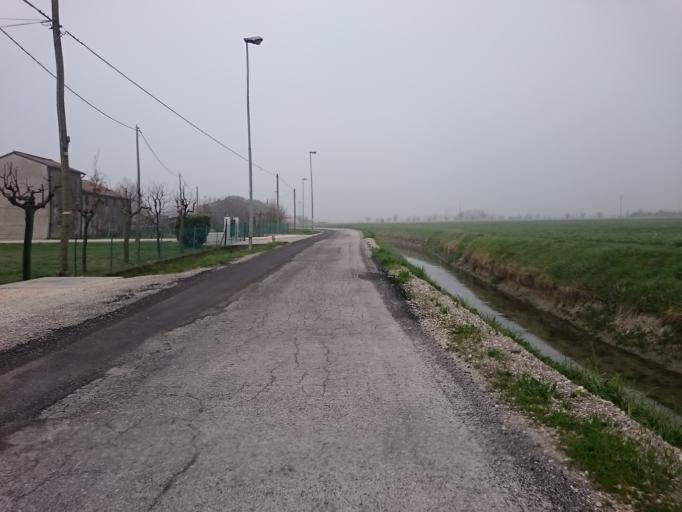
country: IT
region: Veneto
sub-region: Provincia di Padova
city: Masera di Padova
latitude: 45.3006
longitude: 11.8487
